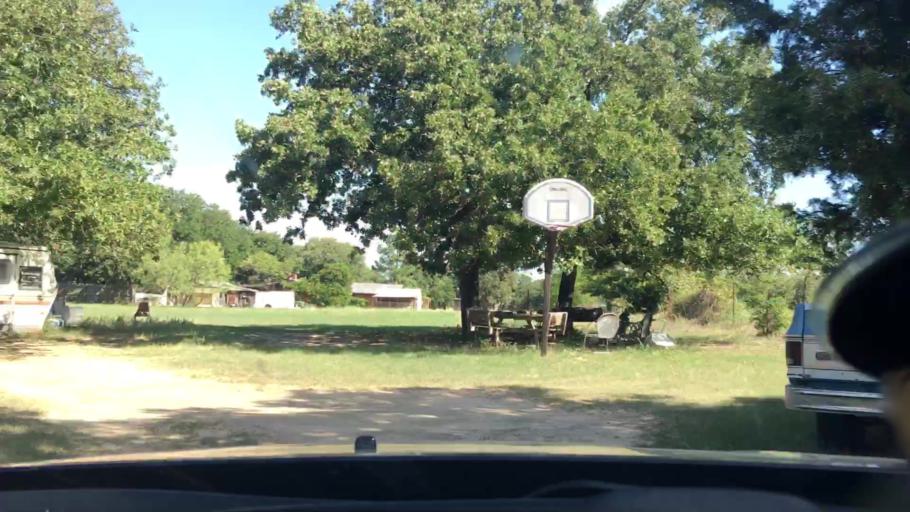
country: US
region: Oklahoma
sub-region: Carter County
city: Ardmore
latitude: 34.1410
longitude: -97.0798
